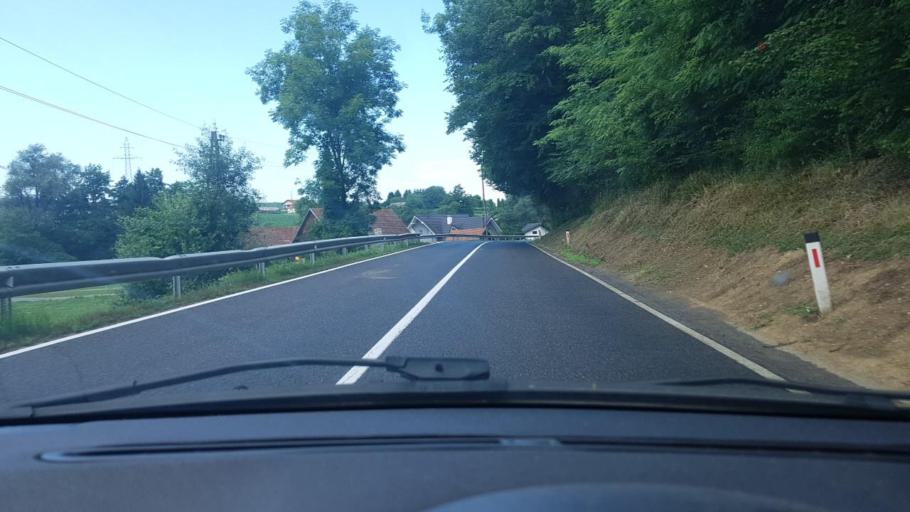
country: SI
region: Sentilj
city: Selnica ob Muri
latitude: 46.6902
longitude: 15.7067
